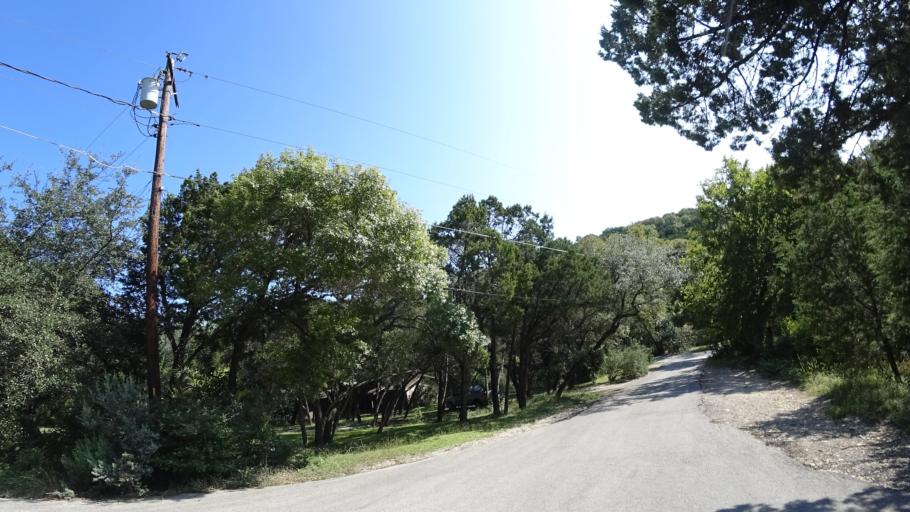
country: US
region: Texas
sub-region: Travis County
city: West Lake Hills
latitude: 30.2945
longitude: -97.8056
